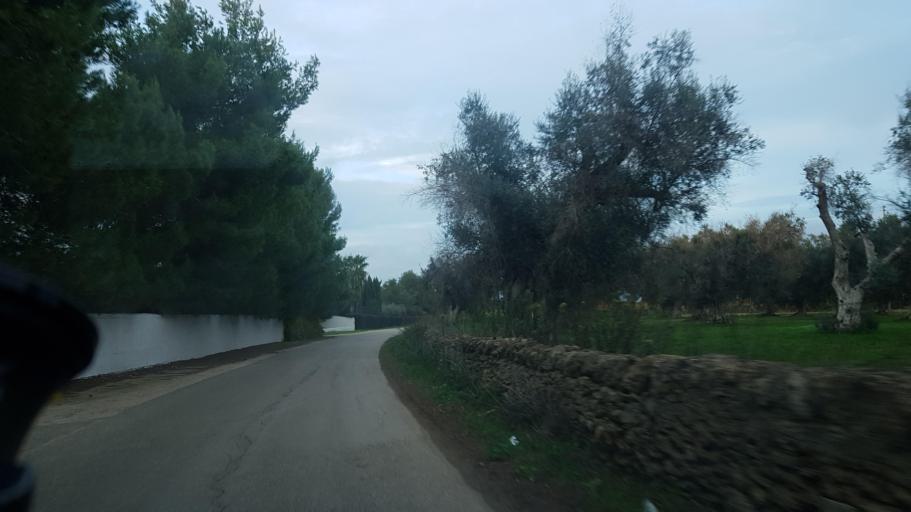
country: IT
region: Apulia
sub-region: Provincia di Brindisi
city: Mesagne
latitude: 40.5460
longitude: 17.7878
